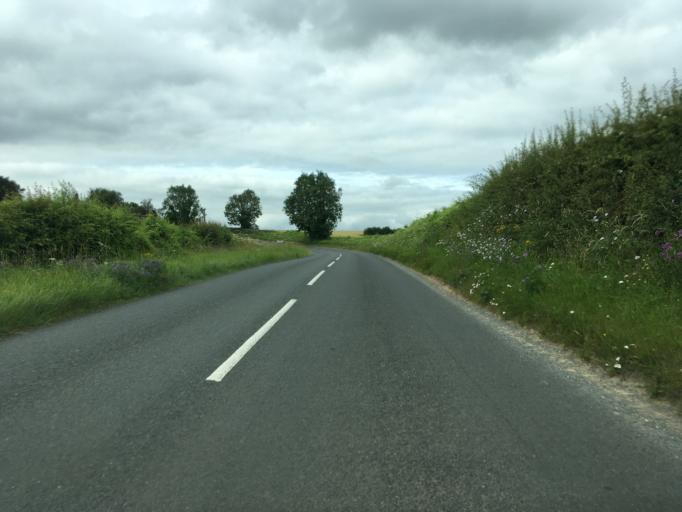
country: GB
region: England
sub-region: Gloucestershire
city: Bourton on the Water
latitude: 51.8820
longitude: -1.7004
